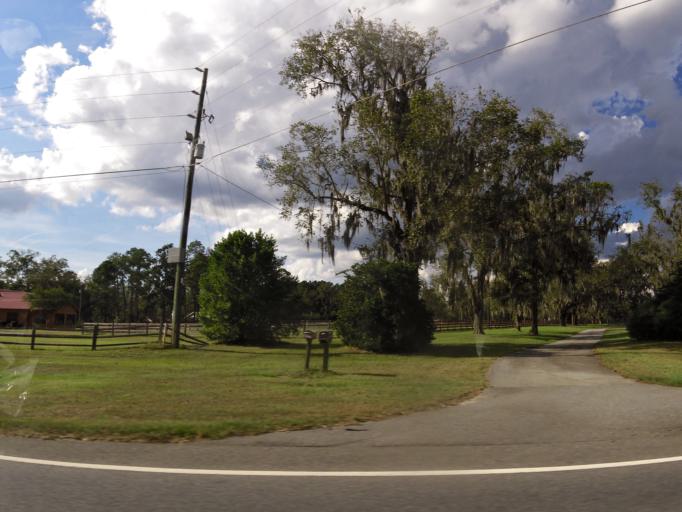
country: US
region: Georgia
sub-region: Lowndes County
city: Remerton
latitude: 30.8025
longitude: -83.3641
